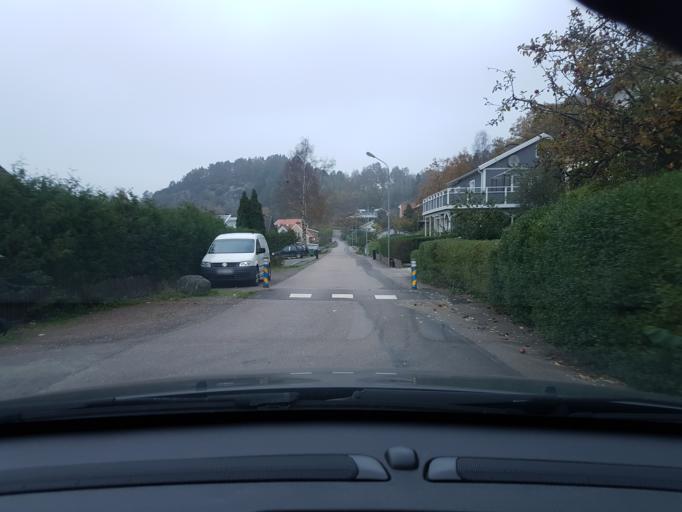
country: SE
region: Vaestra Goetaland
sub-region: Ale Kommun
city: Surte
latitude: 57.8367
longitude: 12.0194
